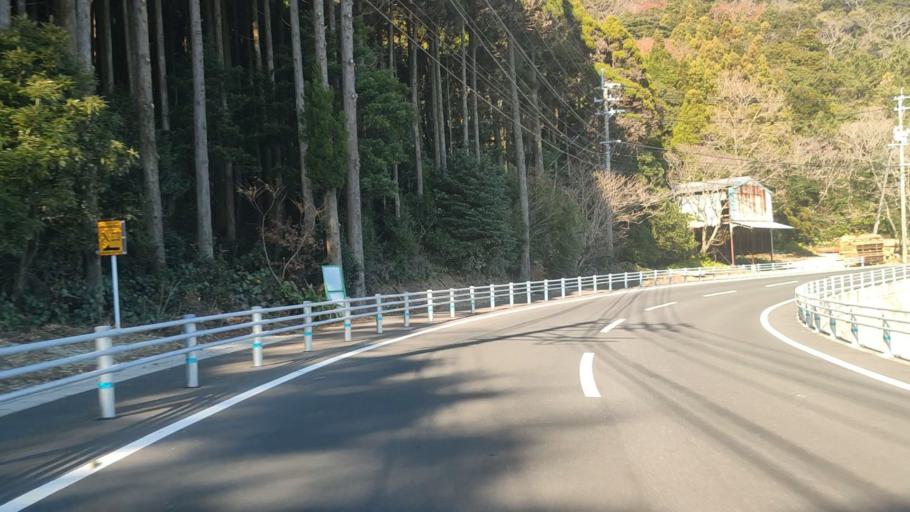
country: JP
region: Oita
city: Saiki
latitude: 32.7961
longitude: 131.8866
